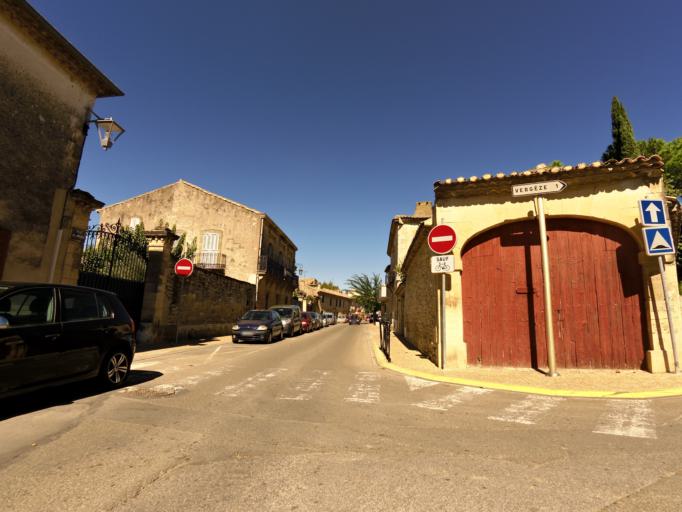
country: FR
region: Languedoc-Roussillon
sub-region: Departement du Gard
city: Codognan
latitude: 43.7308
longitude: 4.2194
